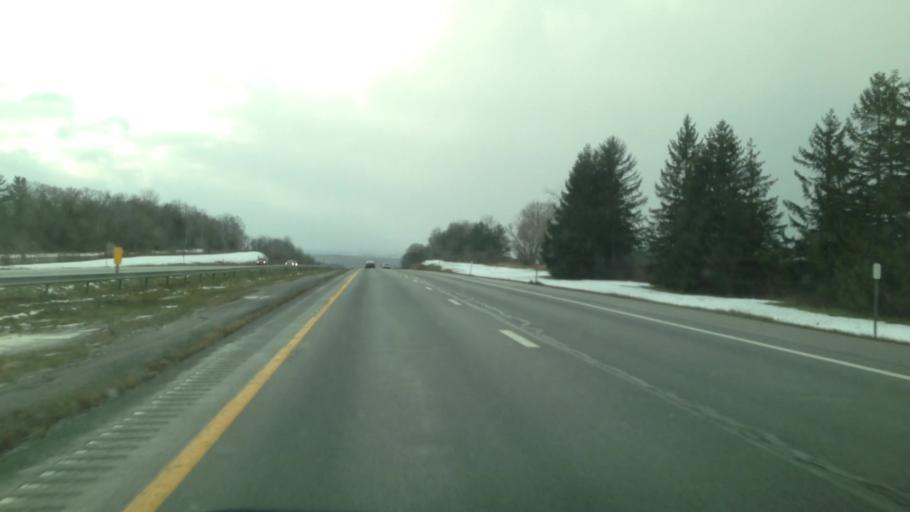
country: US
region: New York
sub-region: Montgomery County
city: Tribes Hill
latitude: 42.9332
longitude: -74.2534
